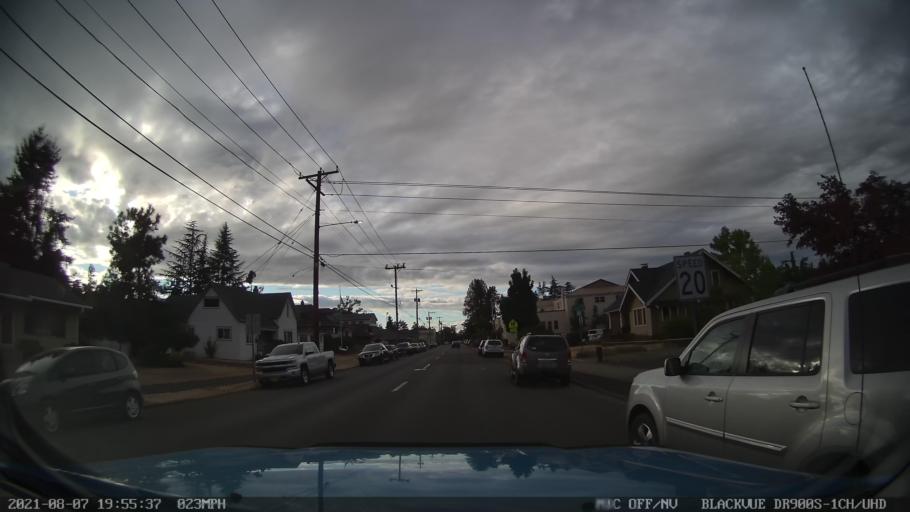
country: US
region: Oregon
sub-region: Marion County
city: Silverton
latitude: 45.0021
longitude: -122.7802
